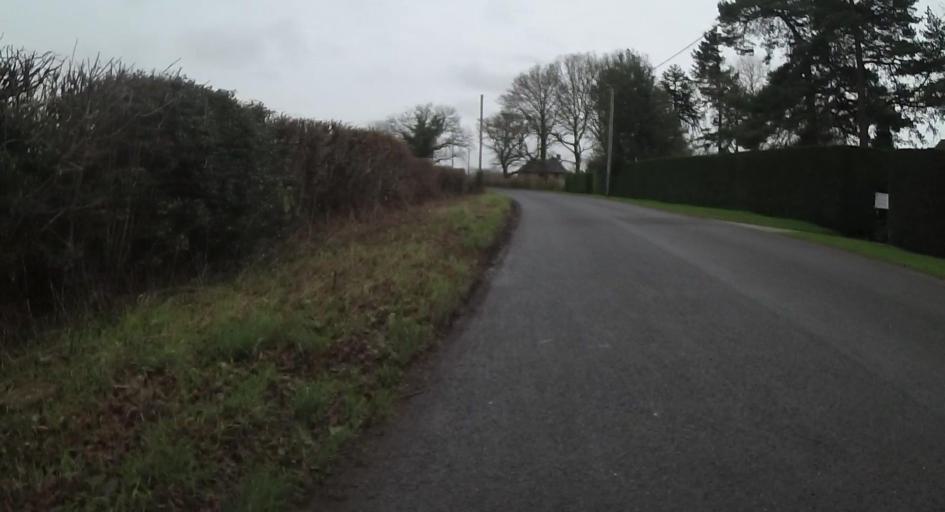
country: GB
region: England
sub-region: Hampshire
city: Four Marks
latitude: 51.1068
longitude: -1.0283
